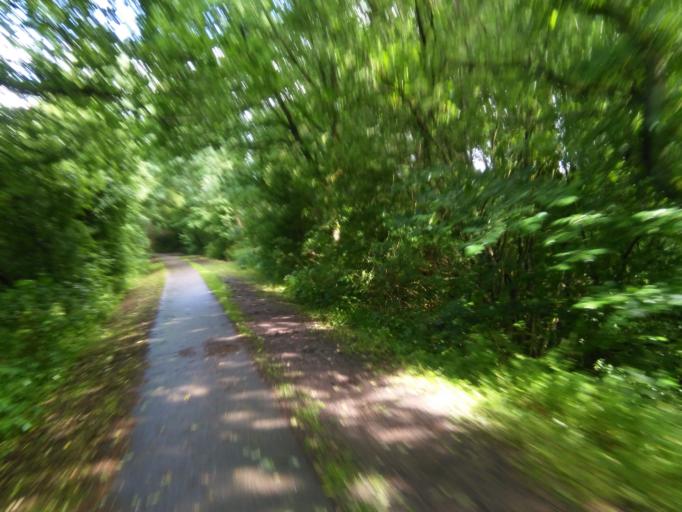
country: DK
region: Central Jutland
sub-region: Horsens Kommune
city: Braedstrup
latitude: 55.9683
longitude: 9.6943
